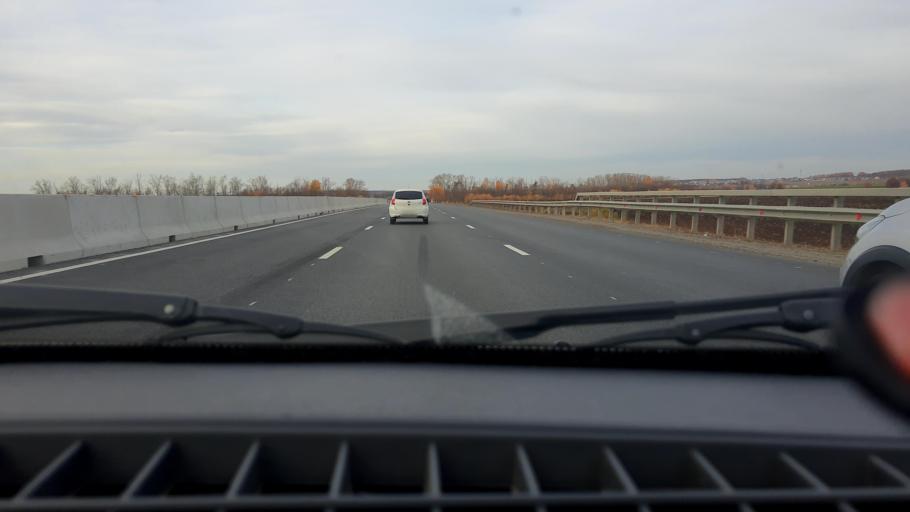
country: RU
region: Bashkortostan
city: Avdon
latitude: 54.6713
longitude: 55.7688
